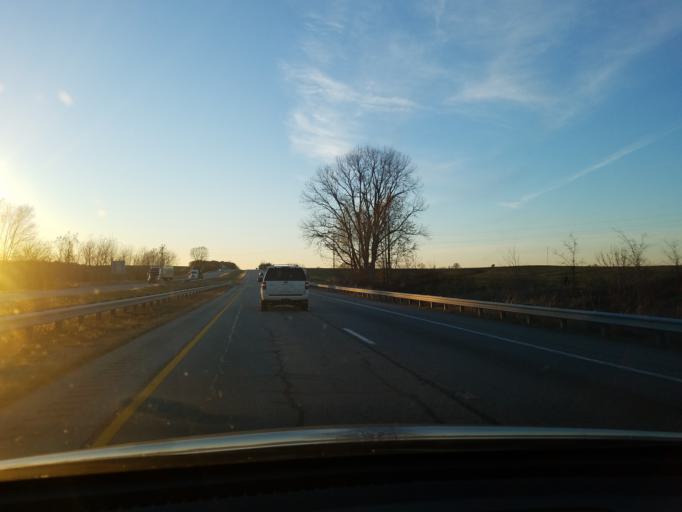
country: US
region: Indiana
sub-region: Posey County
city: Poseyville
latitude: 38.1843
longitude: -87.7906
